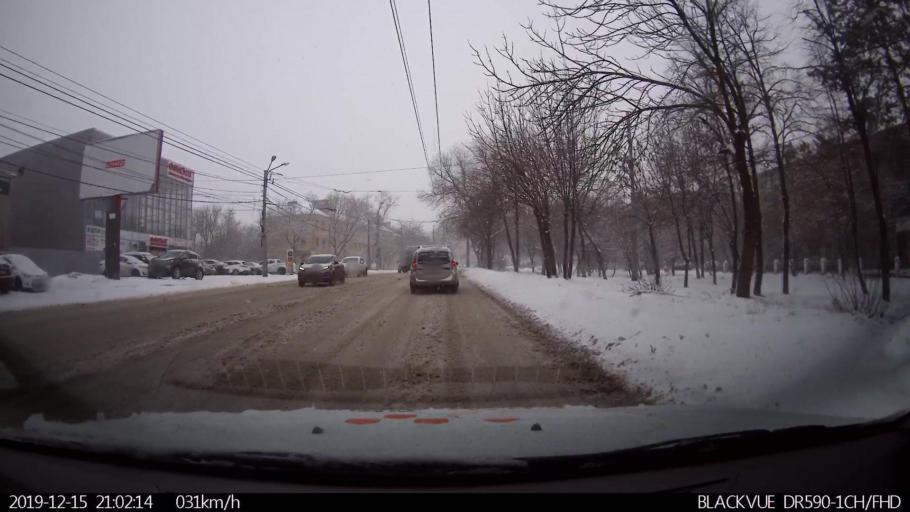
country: RU
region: Nizjnij Novgorod
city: Nizhniy Novgorod
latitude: 56.3071
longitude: 43.9438
